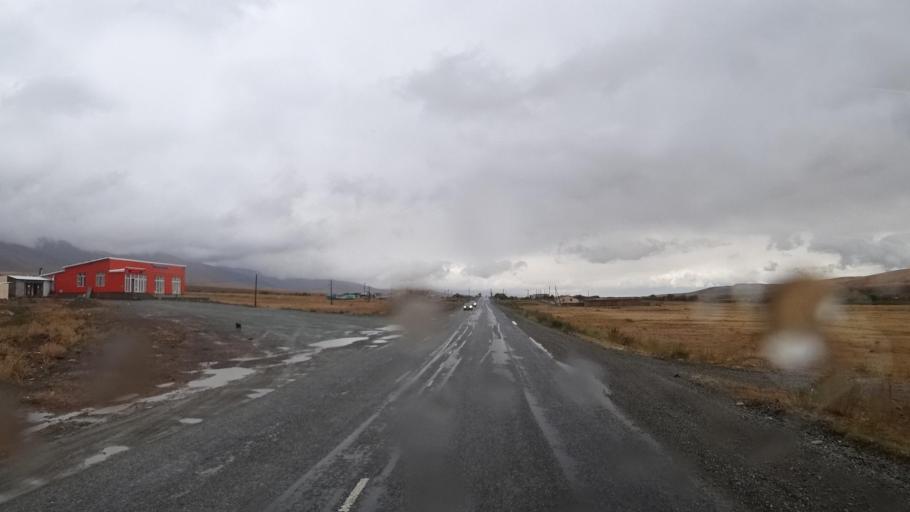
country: KG
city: Sosnovka
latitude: 42.2173
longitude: 73.6886
